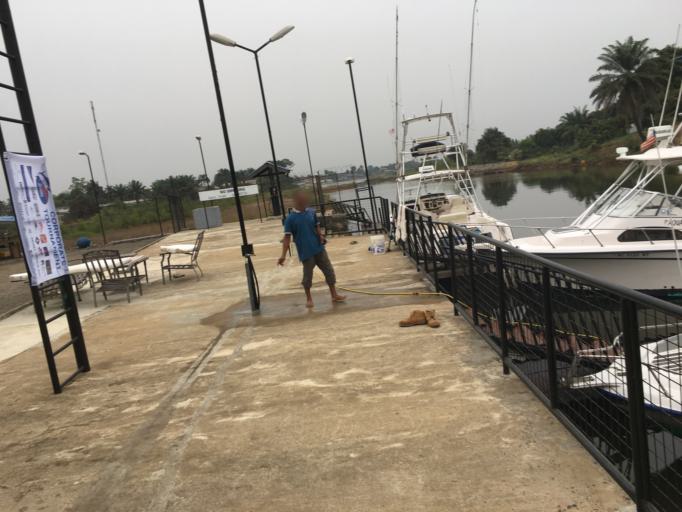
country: LR
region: Montserrado
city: Monrovia
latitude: 6.3945
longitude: -10.7915
